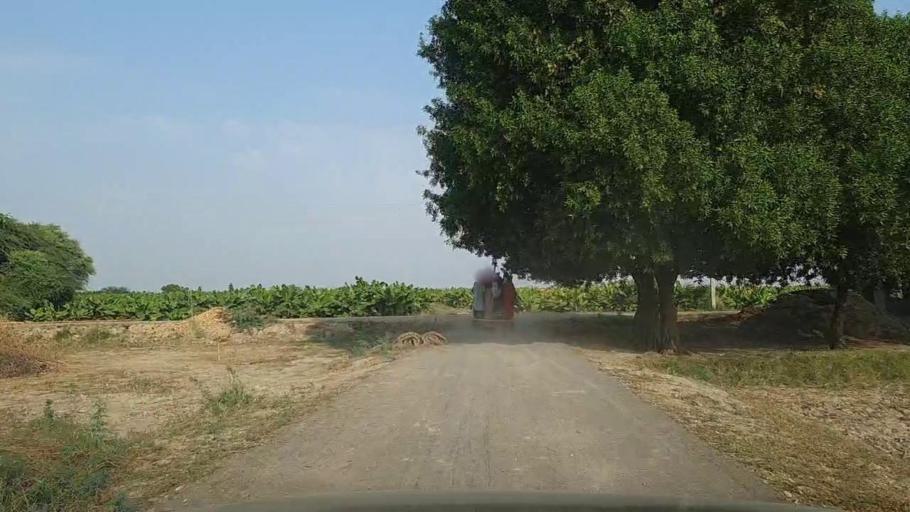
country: PK
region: Sindh
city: Thatta
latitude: 24.6422
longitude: 67.9501
